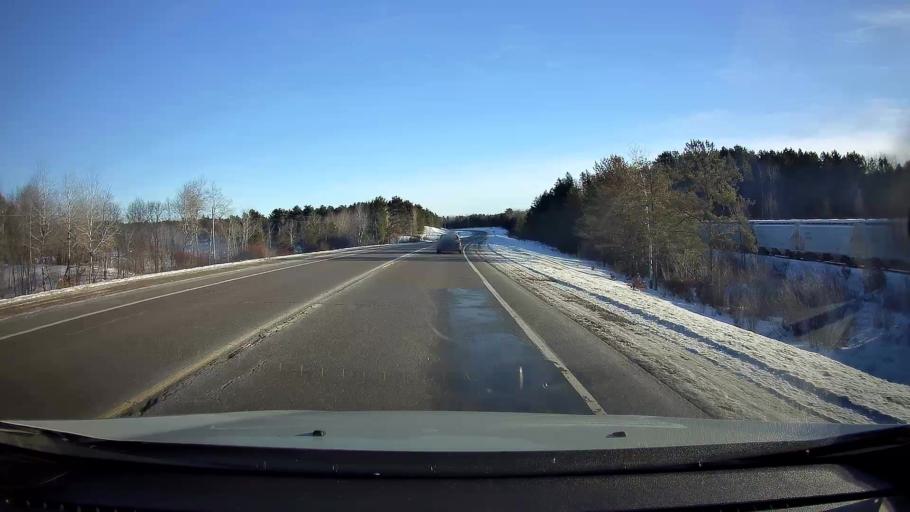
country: US
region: Wisconsin
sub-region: Washburn County
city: Spooner
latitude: 45.9327
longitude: -91.7128
